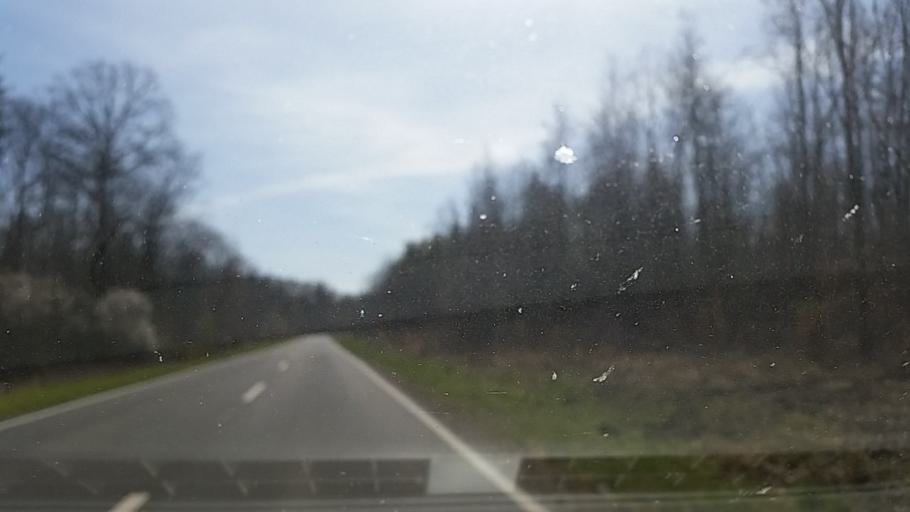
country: DE
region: Lower Saxony
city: Warberg
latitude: 52.1548
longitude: 10.9244
